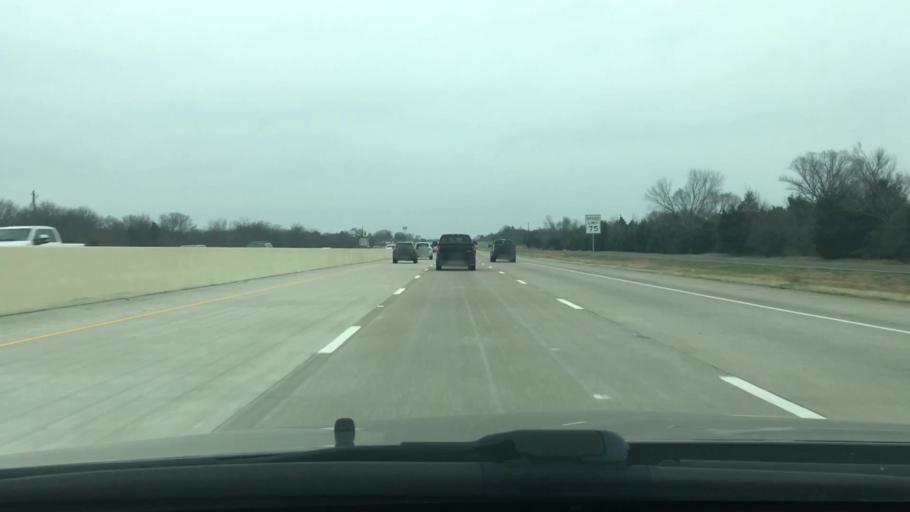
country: US
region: Texas
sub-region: Navarro County
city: Corsicana
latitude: 32.0012
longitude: -96.4310
